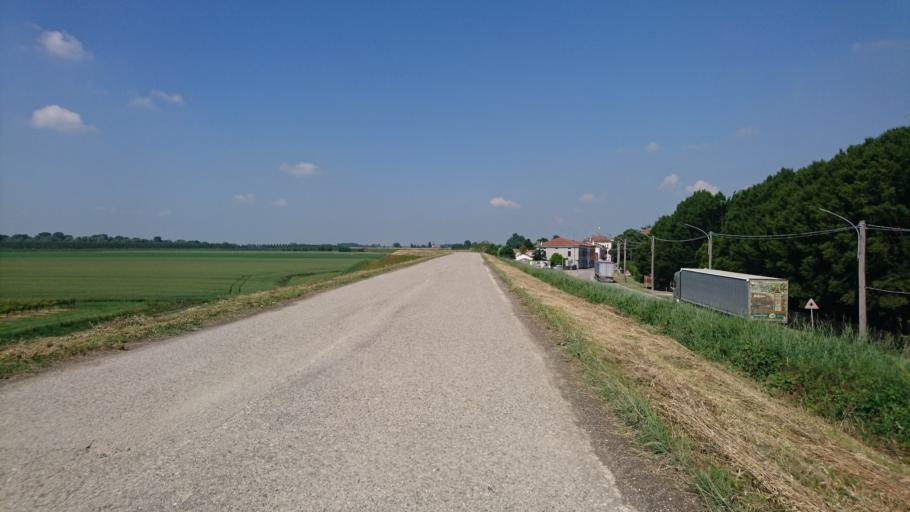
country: IT
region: Lombardy
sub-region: Provincia di Mantova
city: Sustinente
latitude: 45.0672
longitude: 11.0261
